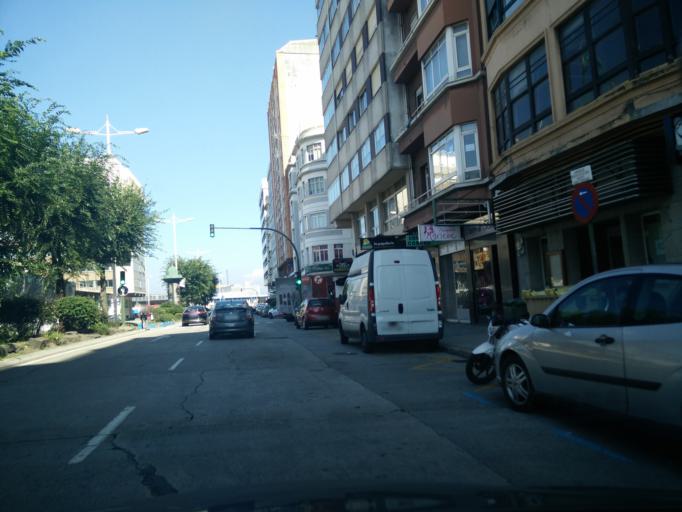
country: ES
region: Galicia
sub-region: Provincia da Coruna
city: A Coruna
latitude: 43.3566
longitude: -8.4012
